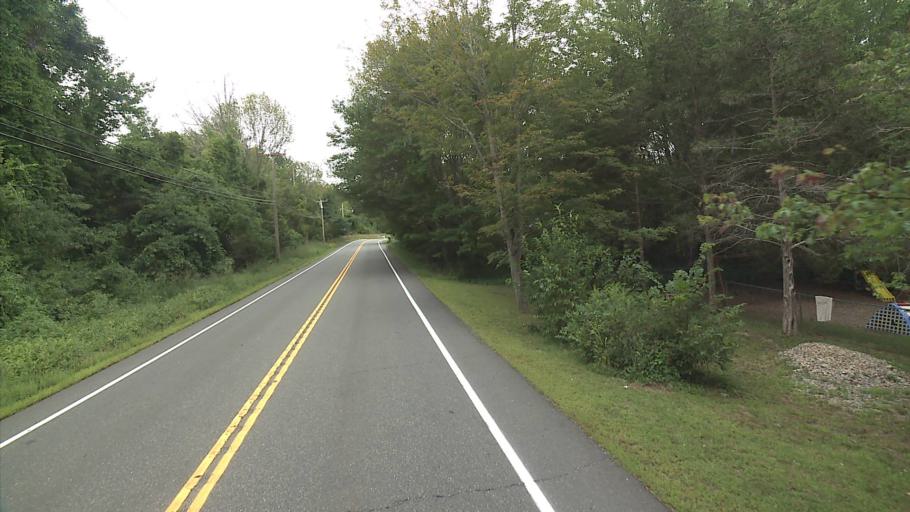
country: US
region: Connecticut
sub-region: New London County
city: Colchester
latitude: 41.4815
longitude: -72.2709
